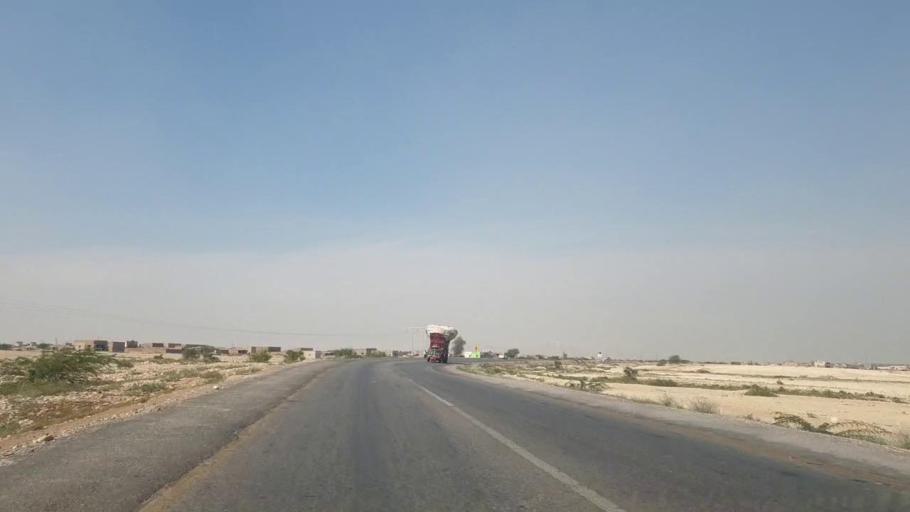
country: PK
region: Sindh
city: Hala
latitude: 25.7981
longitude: 68.2799
